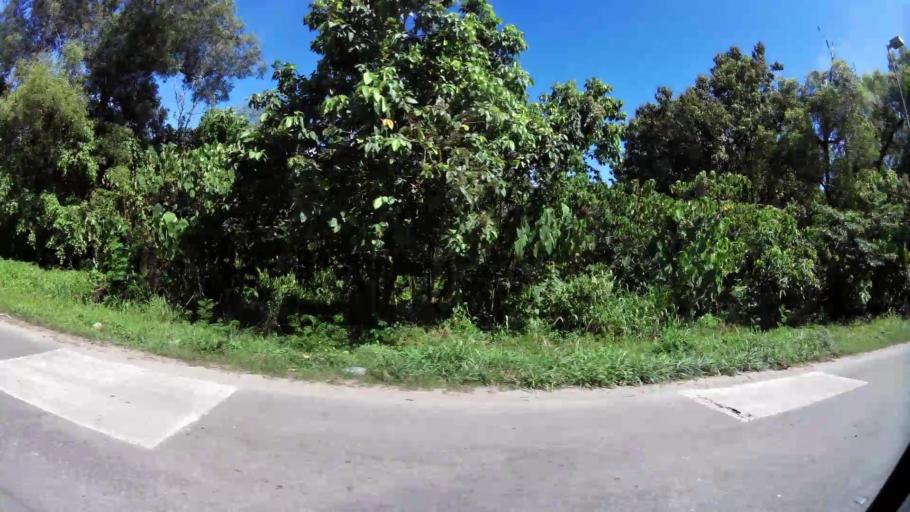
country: BN
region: Brunei and Muara
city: Bandar Seri Begawan
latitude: 5.0239
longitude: 115.0643
